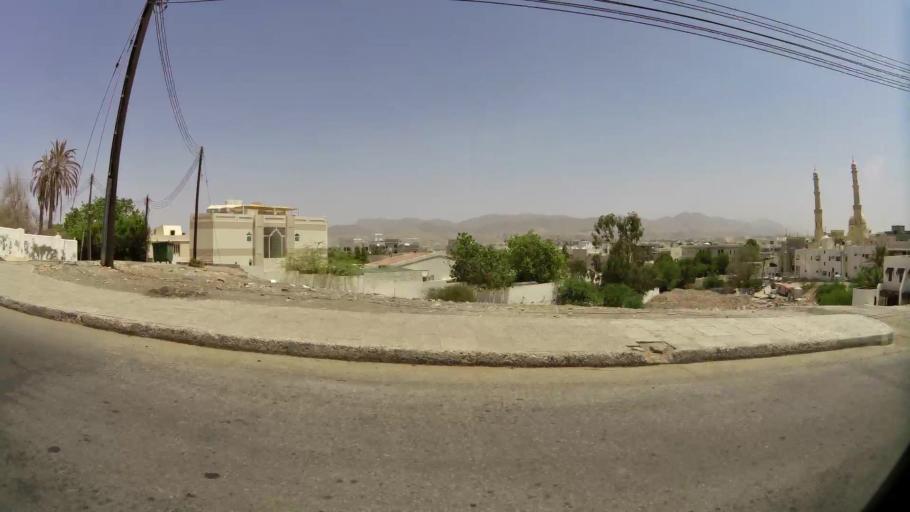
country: OM
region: Muhafazat Masqat
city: Muscat
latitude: 23.6264
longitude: 58.4877
